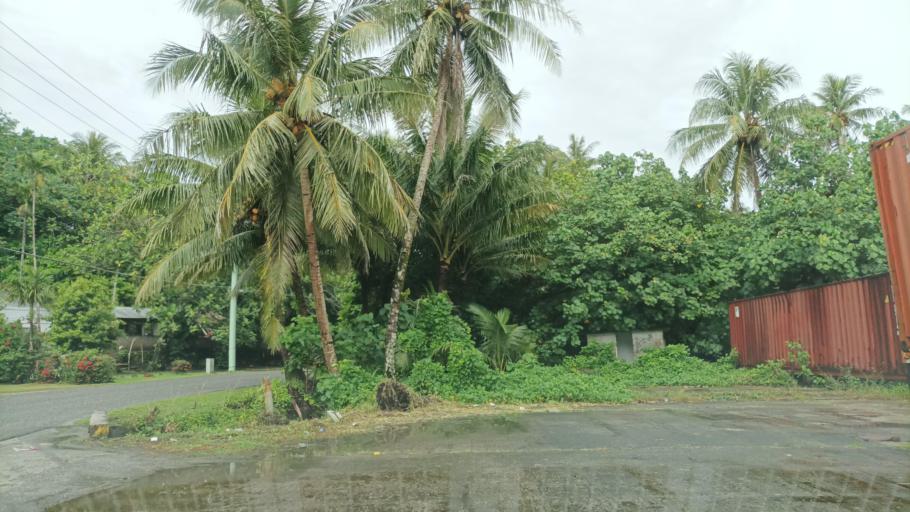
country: FM
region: Kosrae
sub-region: Tafunsak Municipality
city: Tafunsak
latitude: 5.3685
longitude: 162.9950
